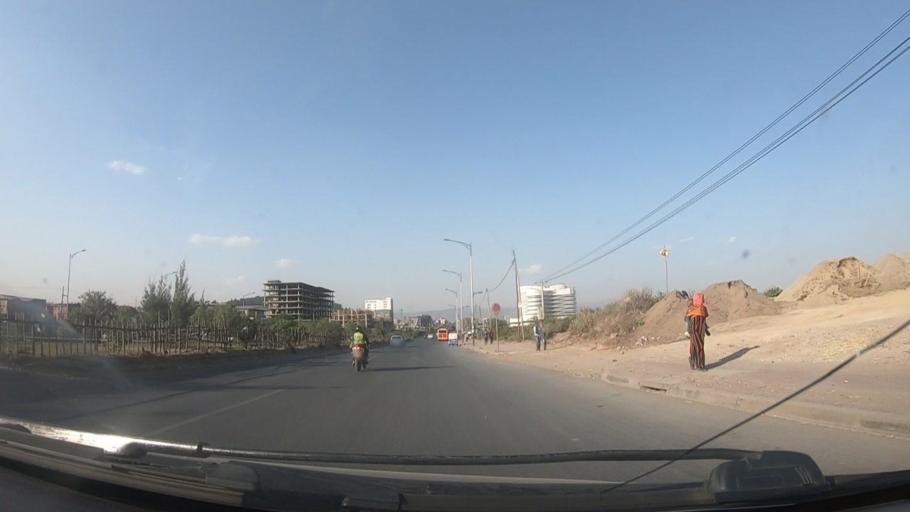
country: ET
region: Adis Abeba
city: Addis Ababa
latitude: 8.9301
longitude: 38.7341
